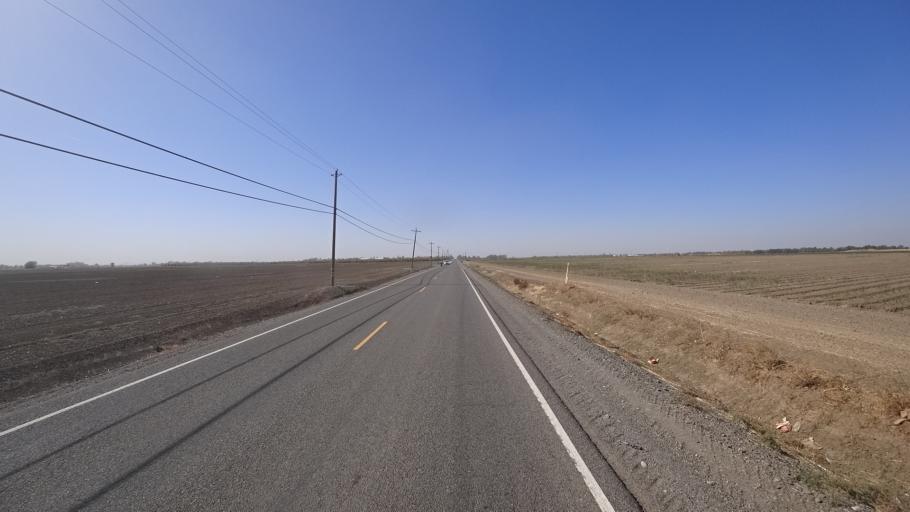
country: US
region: California
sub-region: Yolo County
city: Davis
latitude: 38.5900
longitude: -121.7466
